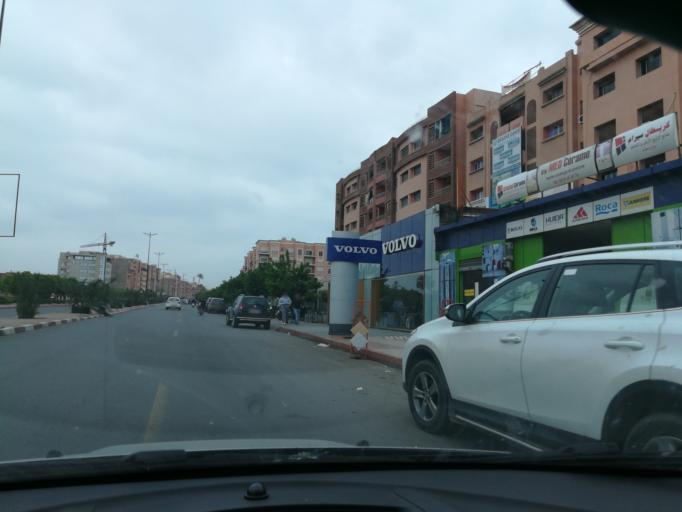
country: MA
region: Marrakech-Tensift-Al Haouz
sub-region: Marrakech
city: Marrakesh
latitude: 31.6474
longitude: -8.0122
